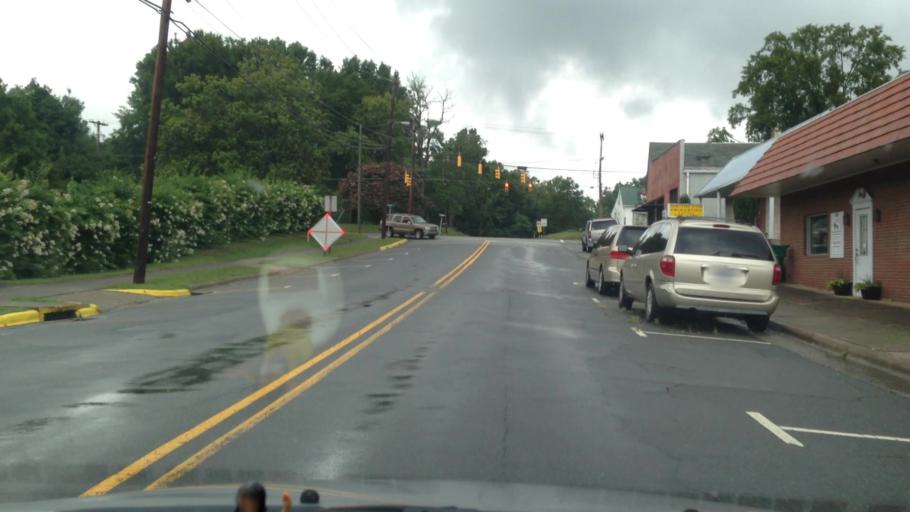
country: US
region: North Carolina
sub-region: Rockingham County
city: Madison
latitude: 36.3879
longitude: -79.9617
